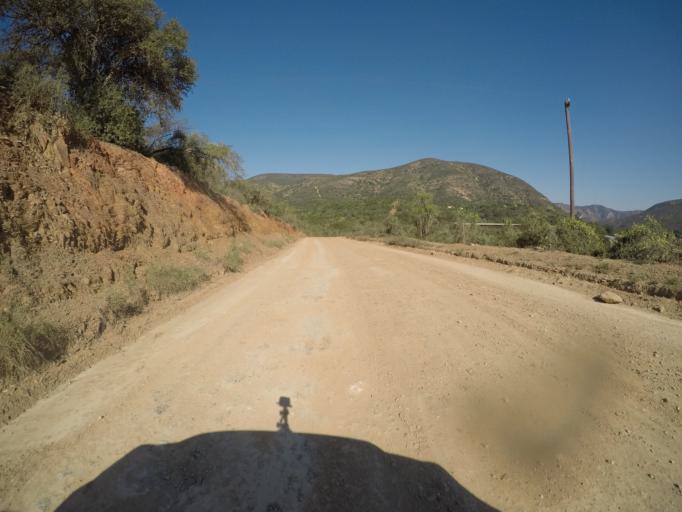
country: ZA
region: Eastern Cape
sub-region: Cacadu District Municipality
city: Kruisfontein
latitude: -33.6648
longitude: 24.5654
